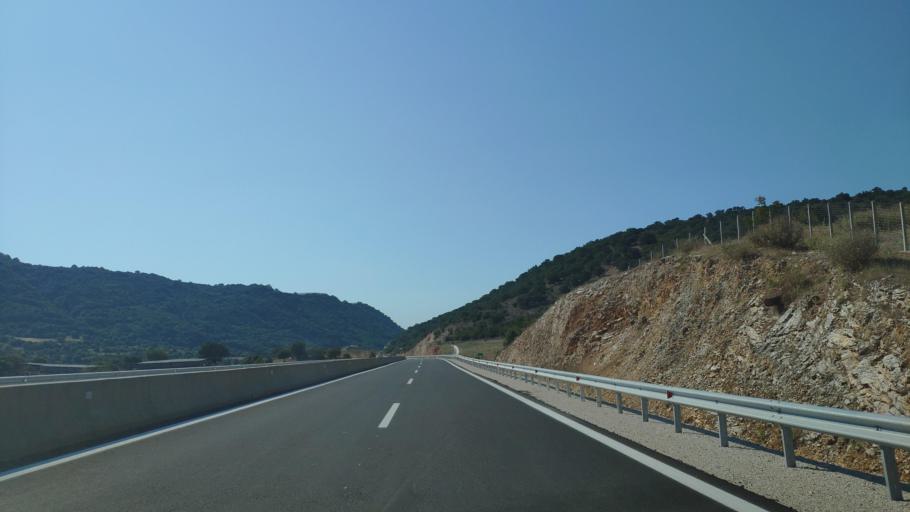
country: GR
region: West Greece
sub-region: Nomos Aitolias kai Akarnanias
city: Katouna
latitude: 38.8443
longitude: 21.1026
